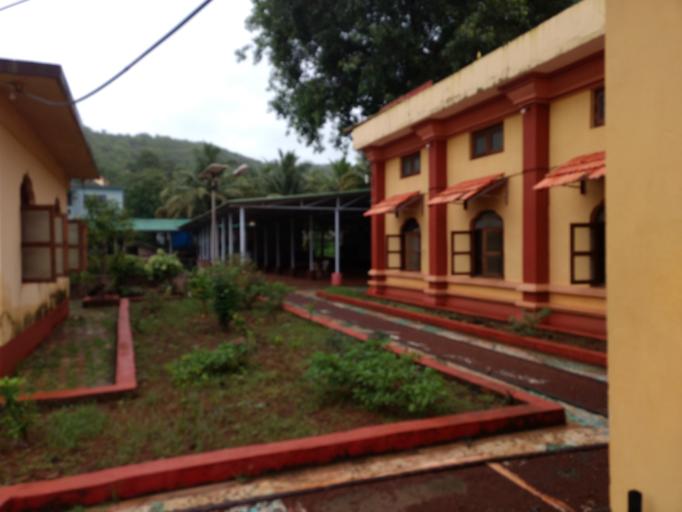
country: IN
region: Maharashtra
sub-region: Ratnagiri
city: Guhagar
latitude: 17.4950
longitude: 73.1880
